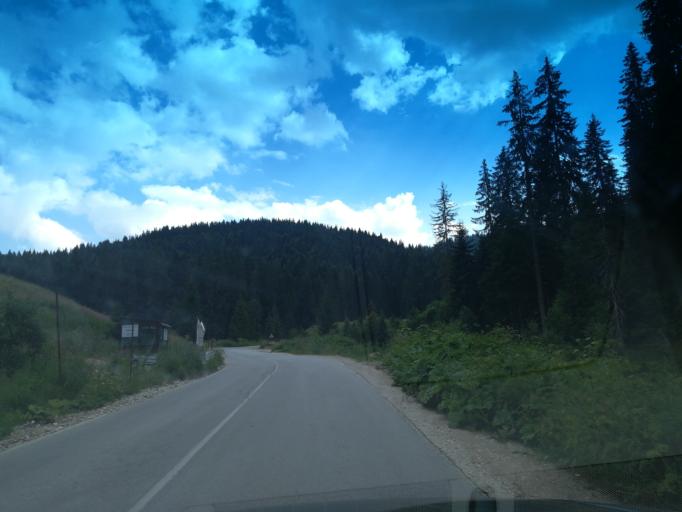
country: BG
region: Smolyan
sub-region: Obshtina Smolyan
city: Smolyan
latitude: 41.6548
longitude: 24.6879
